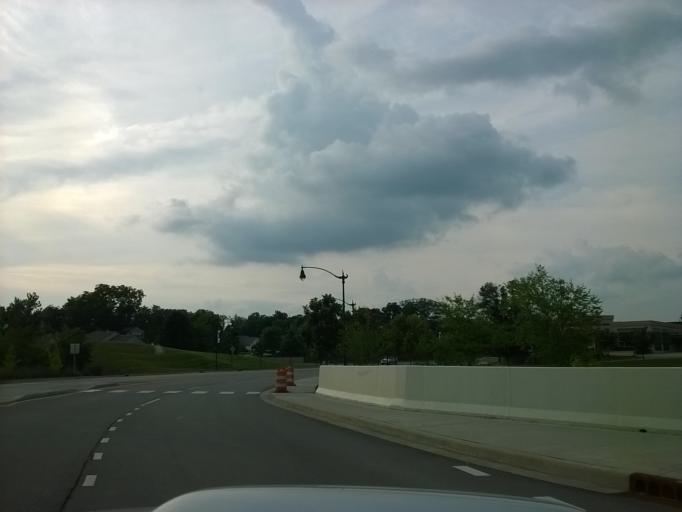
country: US
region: Indiana
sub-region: Hamilton County
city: Carmel
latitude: 39.9927
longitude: -86.1282
